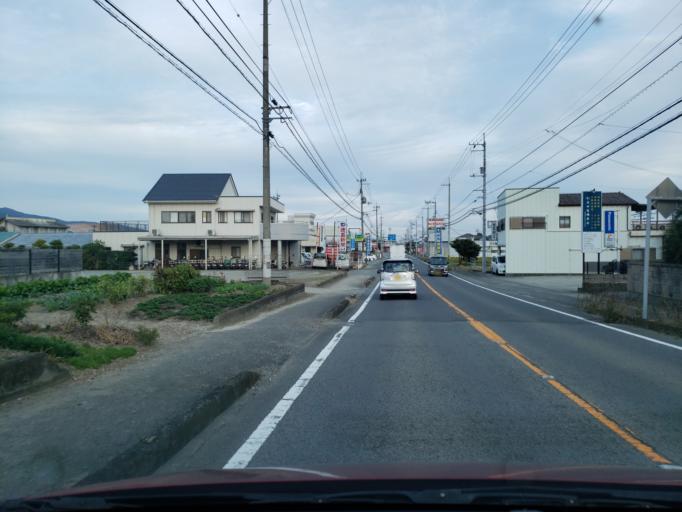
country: JP
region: Tokushima
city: Kamojimacho-jogejima
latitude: 34.0974
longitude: 134.3229
